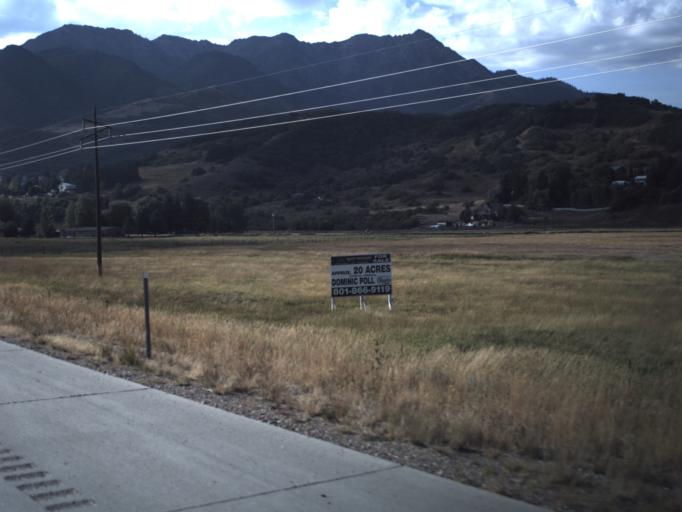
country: US
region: Utah
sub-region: Morgan County
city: Mountain Green
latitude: 41.1391
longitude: -111.8143
